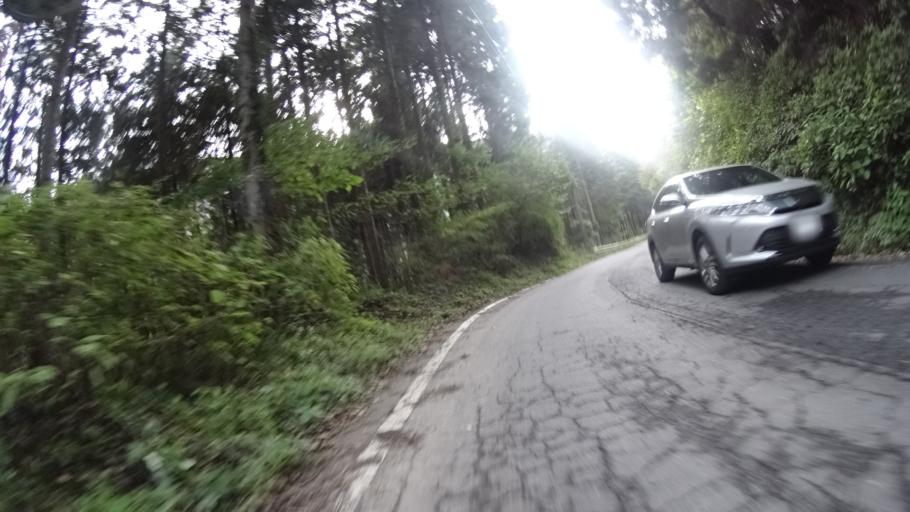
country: JP
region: Yamanashi
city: Uenohara
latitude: 35.6831
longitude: 139.0982
